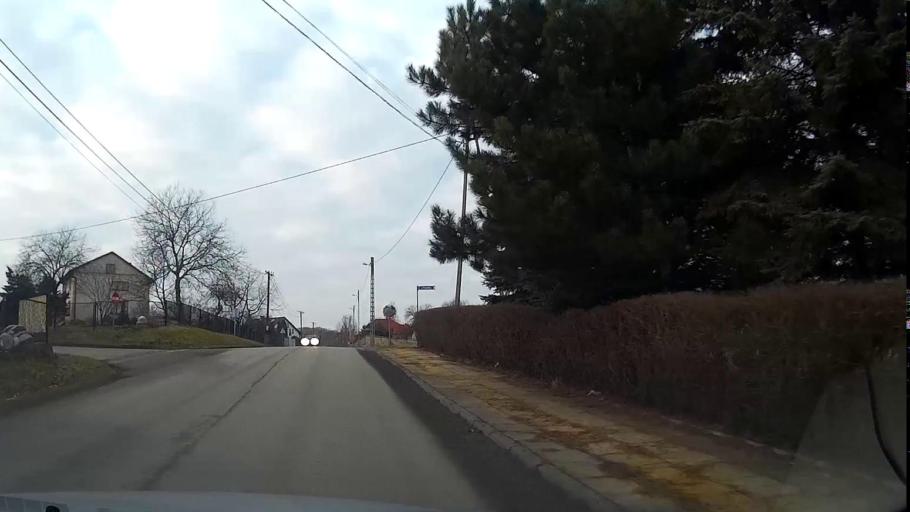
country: PL
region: Lesser Poland Voivodeship
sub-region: Powiat chrzanowski
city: Alwernia
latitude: 50.0642
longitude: 19.5463
